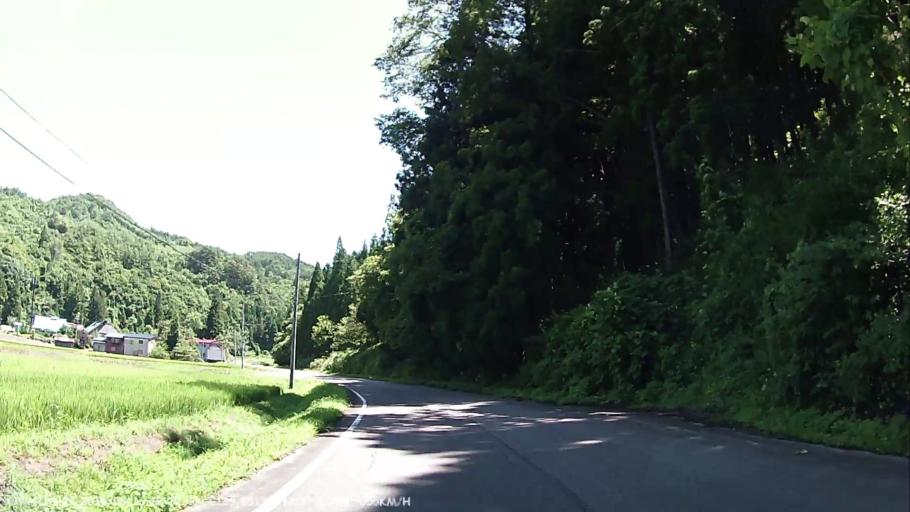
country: JP
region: Fukushima
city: Kitakata
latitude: 37.4172
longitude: 139.8515
